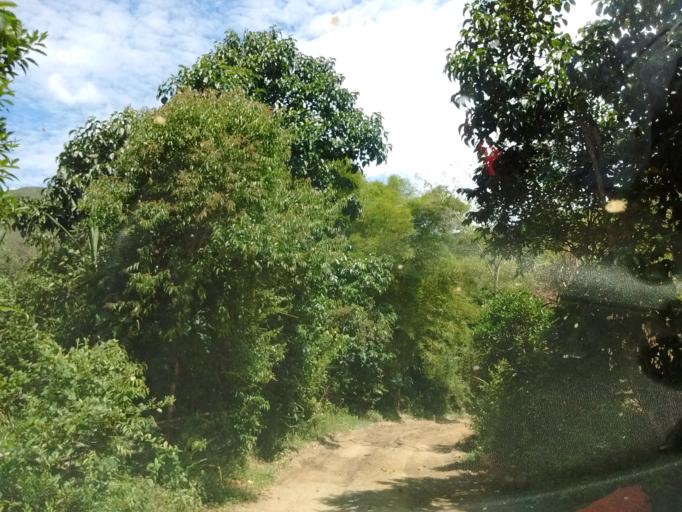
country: CO
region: Cauca
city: Villa Rica
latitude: 2.6543
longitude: -76.7685
